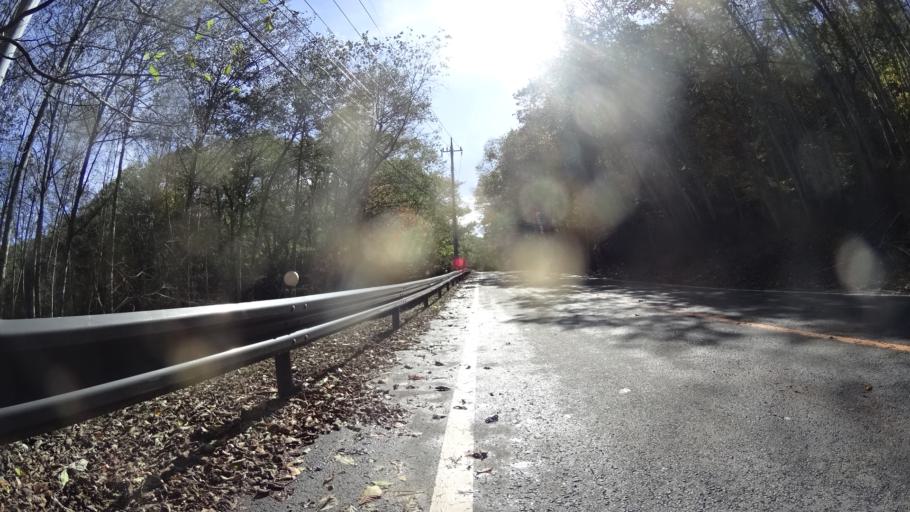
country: JP
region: Yamanashi
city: Enzan
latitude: 35.7866
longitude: 138.7996
